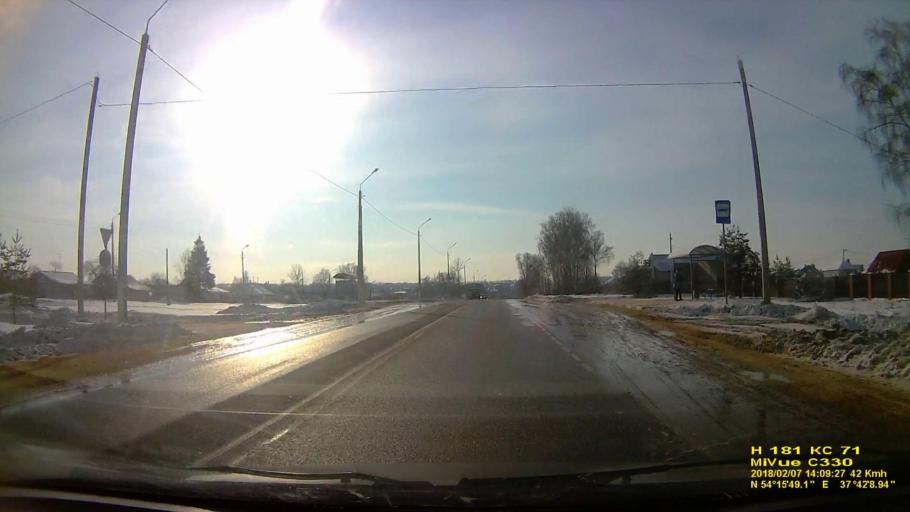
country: RU
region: Tula
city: Gorelki
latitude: 54.2635
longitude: 37.7022
